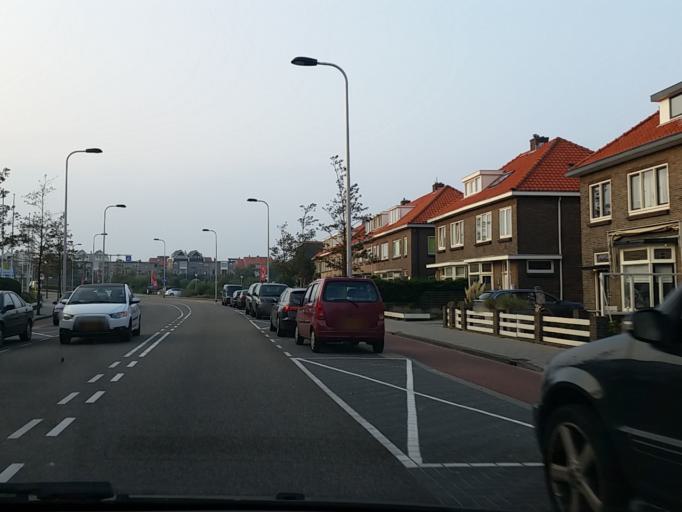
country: NL
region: South Holland
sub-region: Gemeente Noordwijk
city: Noordwijk-Binnen
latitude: 52.2429
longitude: 4.4442
